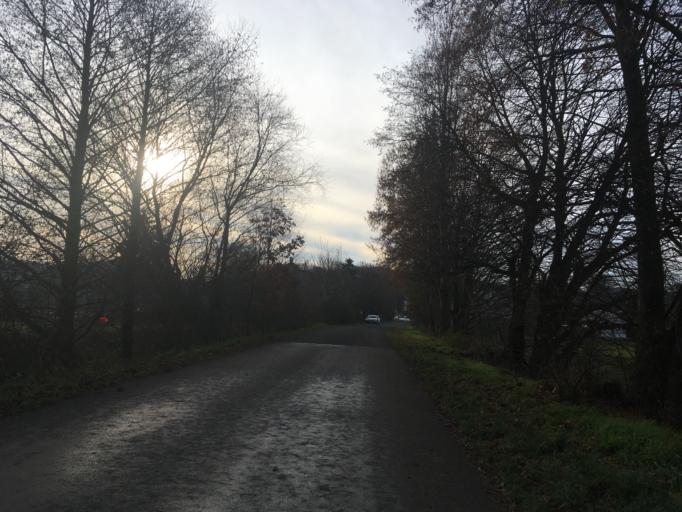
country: DE
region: Brandenburg
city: Falkenberg
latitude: 52.8087
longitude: 13.9635
